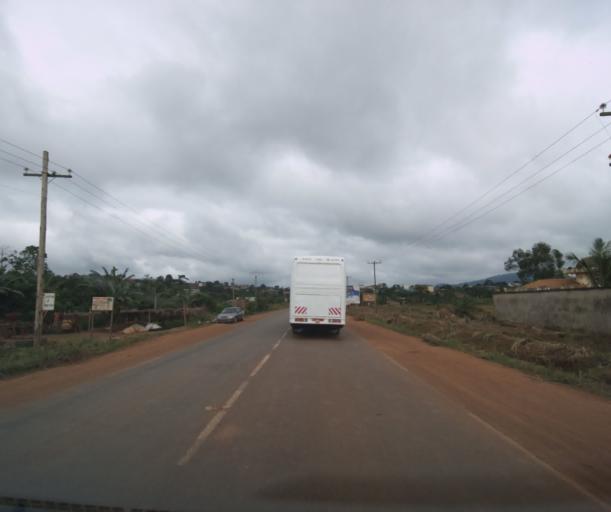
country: CM
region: Centre
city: Yaounde
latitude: 3.7945
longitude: 11.4858
